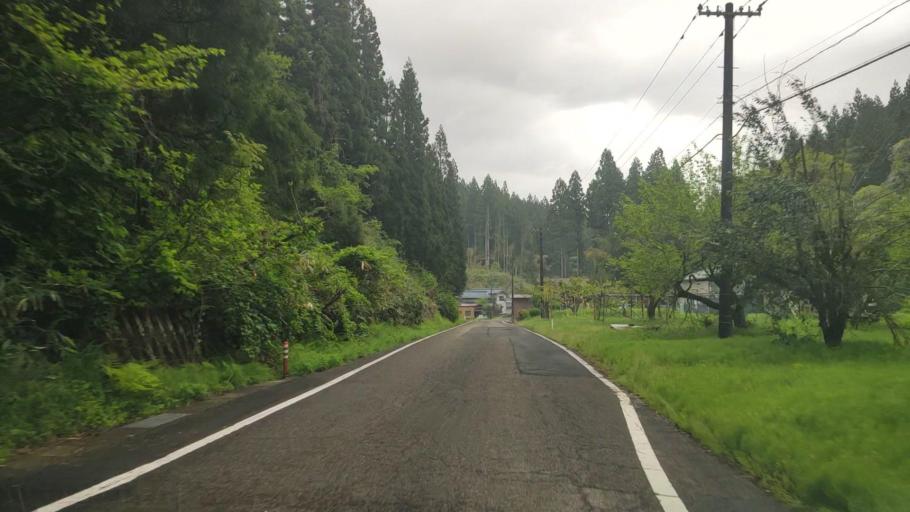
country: JP
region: Niigata
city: Gosen
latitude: 37.7198
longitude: 139.1270
